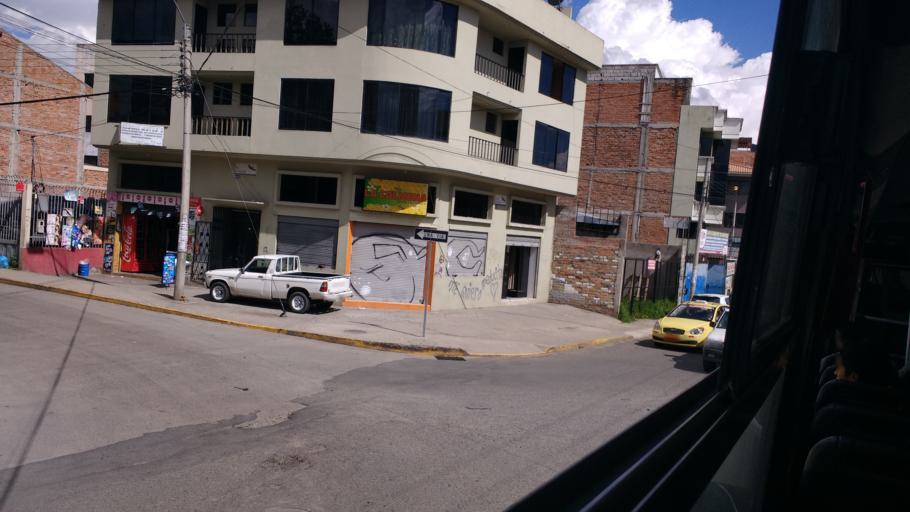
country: EC
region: Azuay
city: Cuenca
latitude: -2.8991
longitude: -79.0251
